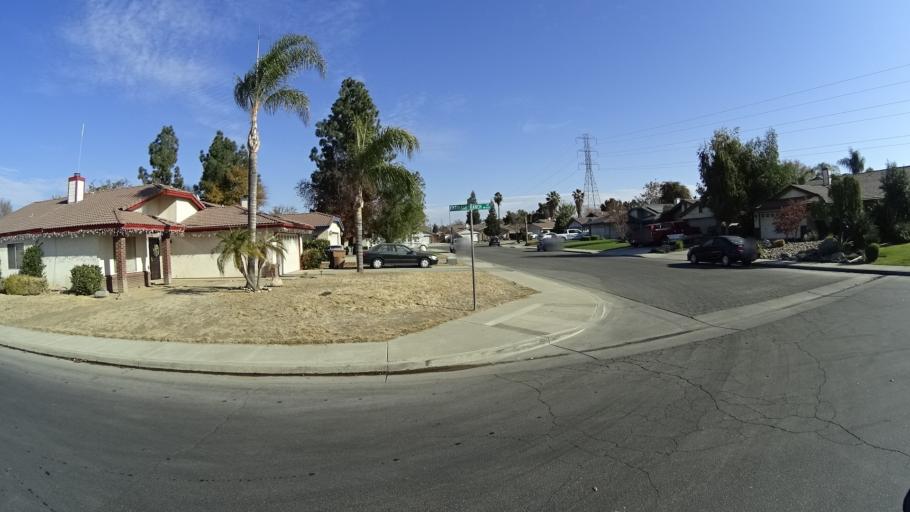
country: US
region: California
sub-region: Kern County
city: Greenacres
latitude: 35.3984
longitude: -119.0878
